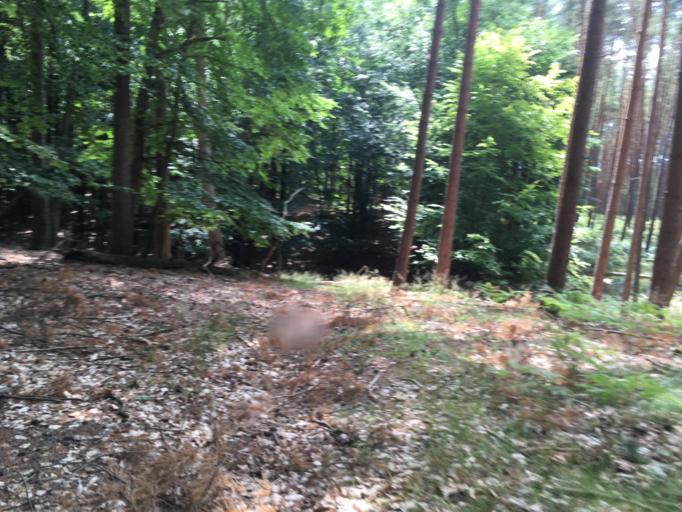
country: DE
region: Brandenburg
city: Althuttendorf
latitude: 52.9407
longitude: 13.7718
